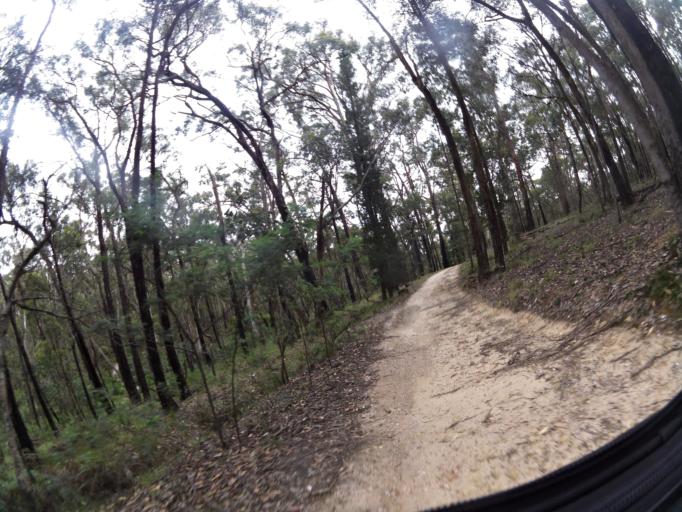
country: AU
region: Victoria
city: Brown Hill
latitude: -37.4901
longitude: 143.9064
